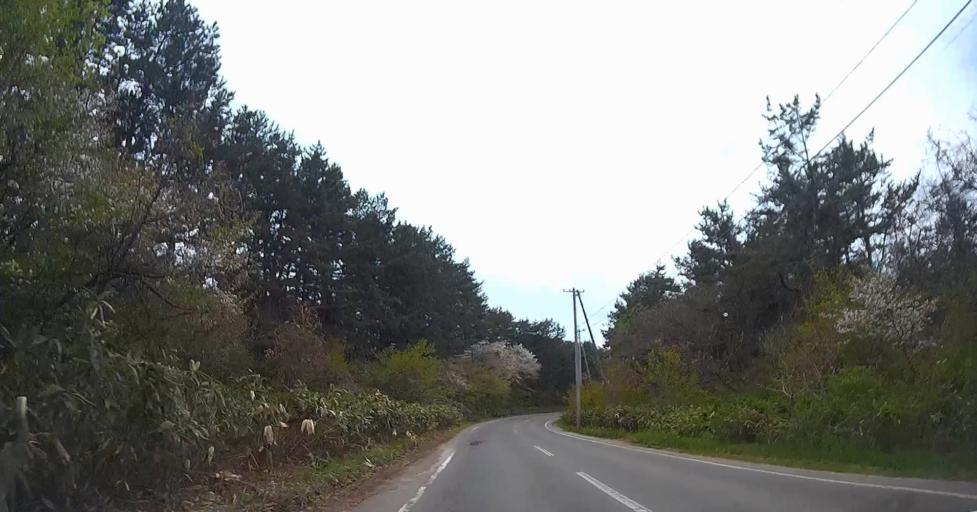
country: JP
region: Aomori
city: Shimokizukuri
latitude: 40.9367
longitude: 140.3363
